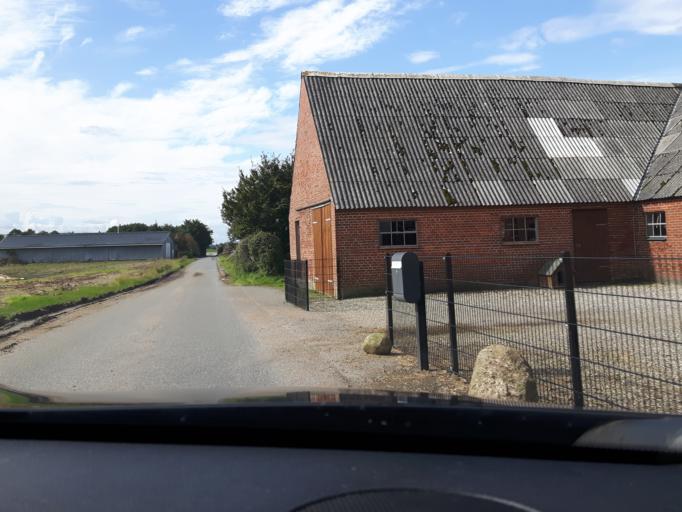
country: DK
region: South Denmark
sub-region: Fredericia Kommune
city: Fredericia
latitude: 55.6006
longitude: 9.7641
